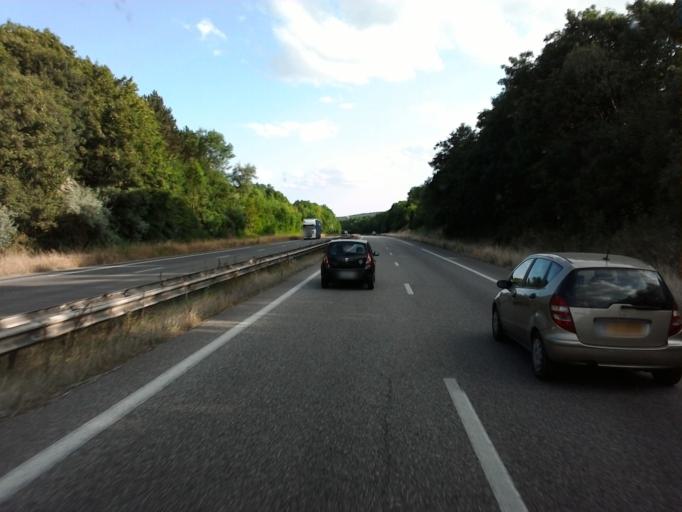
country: FR
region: Lorraine
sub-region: Departement de Meurthe-et-Moselle
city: Richardmenil
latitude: 48.6004
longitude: 6.1720
